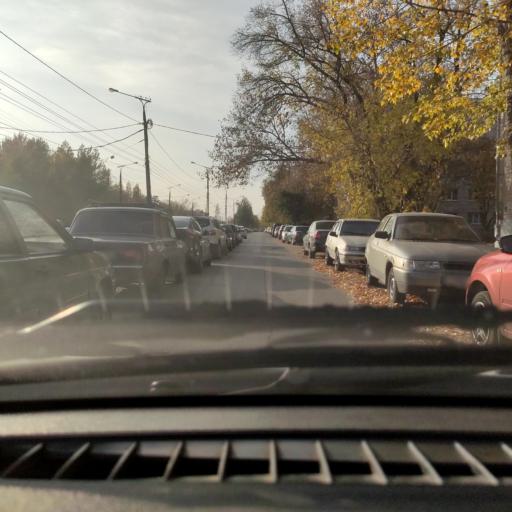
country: RU
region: Samara
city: Tol'yatti
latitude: 53.4986
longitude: 49.3957
